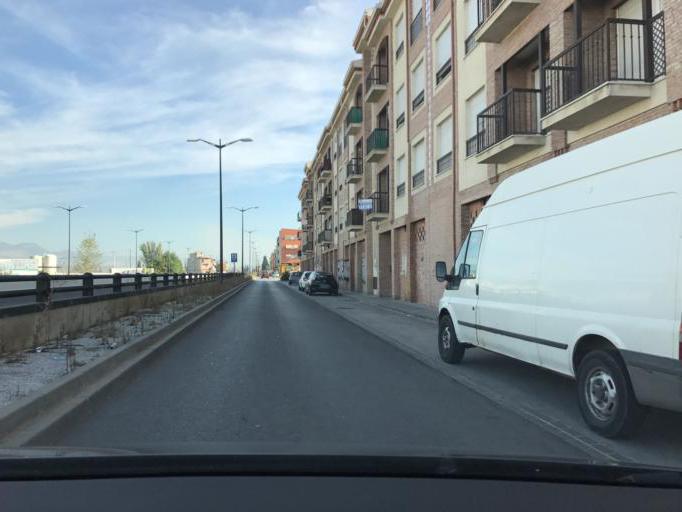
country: ES
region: Andalusia
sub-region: Provincia de Granada
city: Atarfe
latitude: 37.1924
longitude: -3.7152
